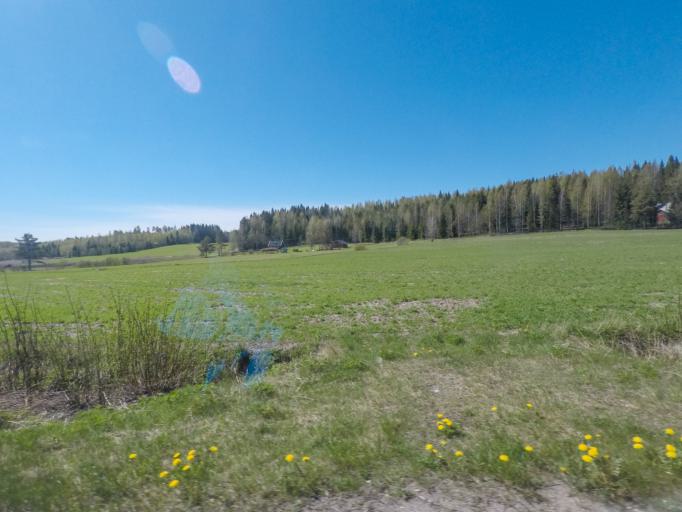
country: FI
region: Uusimaa
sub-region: Helsinki
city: Sammatti
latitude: 60.3971
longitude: 23.8159
